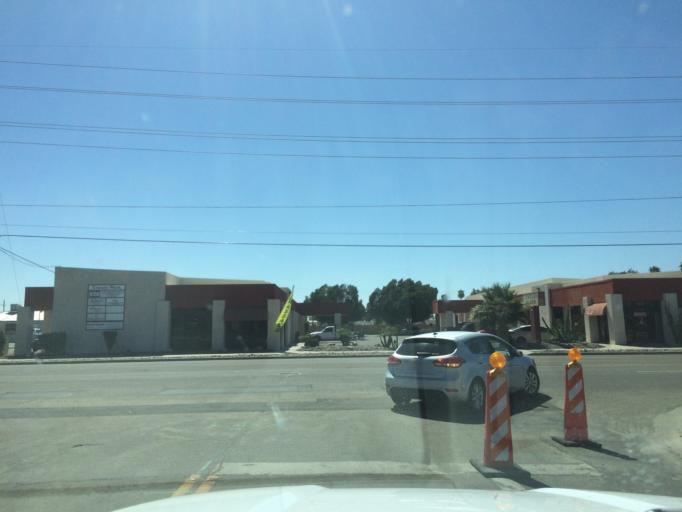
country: US
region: Arizona
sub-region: Yuma County
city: Yuma
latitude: 32.6842
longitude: -114.6227
